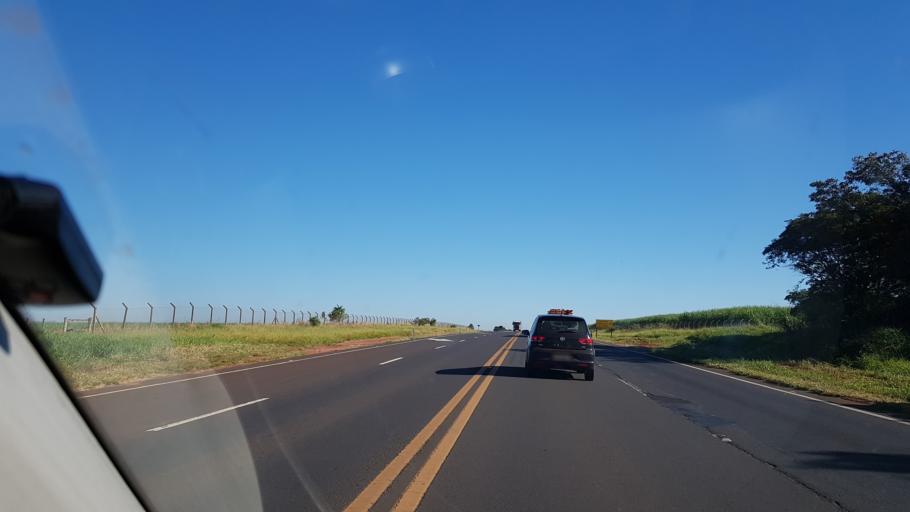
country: BR
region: Sao Paulo
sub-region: Assis
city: Assis
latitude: -22.5978
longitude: -50.4839
